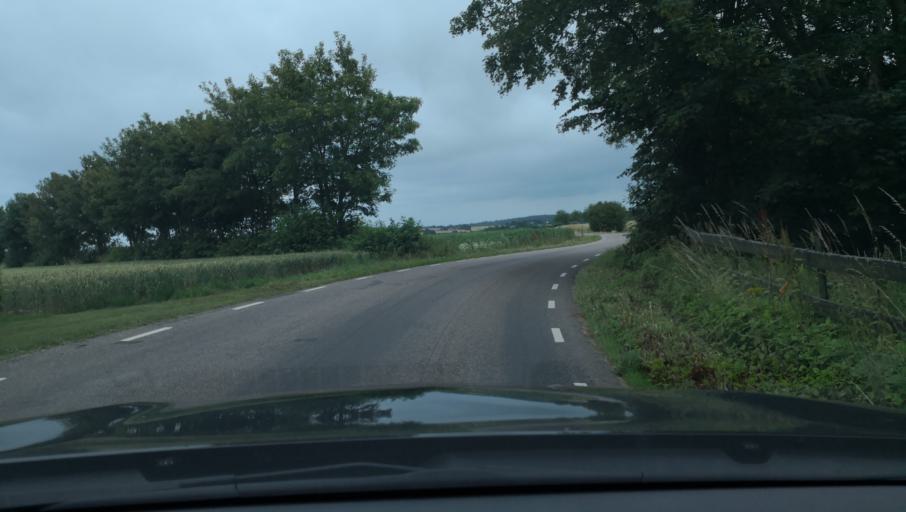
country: SE
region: Skane
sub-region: Simrishamns Kommun
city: Kivik
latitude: 55.6707
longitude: 14.2037
